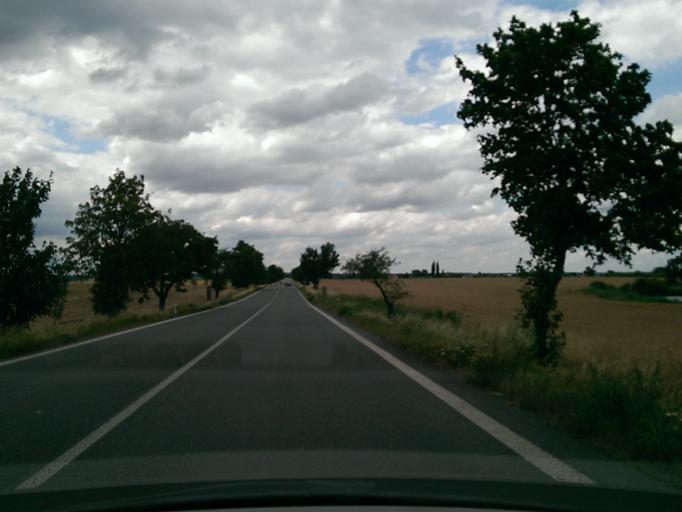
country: CZ
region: Central Bohemia
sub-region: Okres Nymburk
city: Nymburk
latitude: 50.2261
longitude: 15.0264
